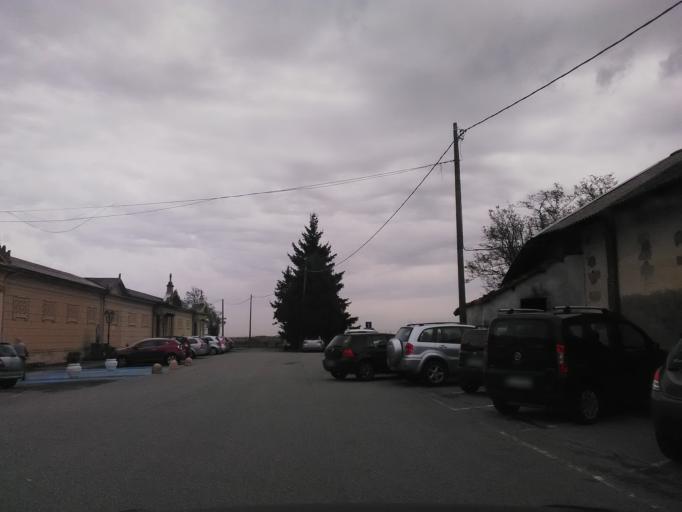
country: IT
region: Piedmont
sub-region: Provincia di Vercelli
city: San Germano Vercellese
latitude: 45.3504
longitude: 8.2533
